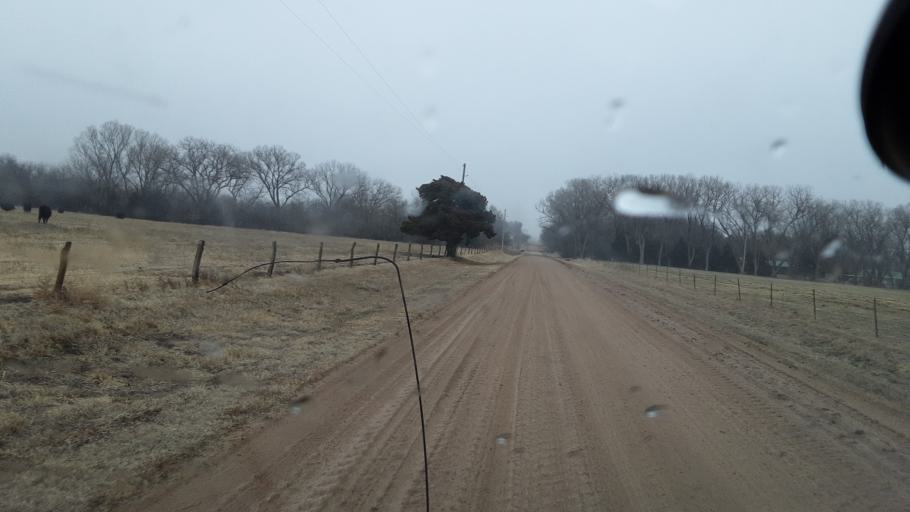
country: US
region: Kansas
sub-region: Reno County
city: South Hutchinson
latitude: 37.9555
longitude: -98.0250
